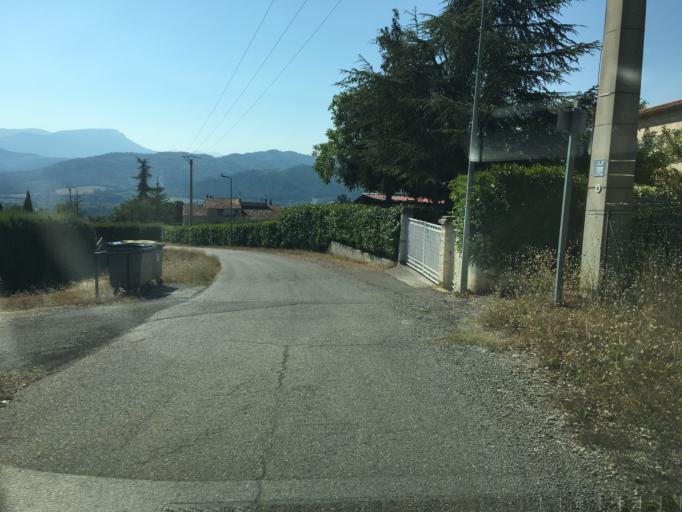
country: FR
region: Provence-Alpes-Cote d'Azur
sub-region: Departement des Alpes-de-Haute-Provence
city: Mallemoisson
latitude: 44.0529
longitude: 6.1342
